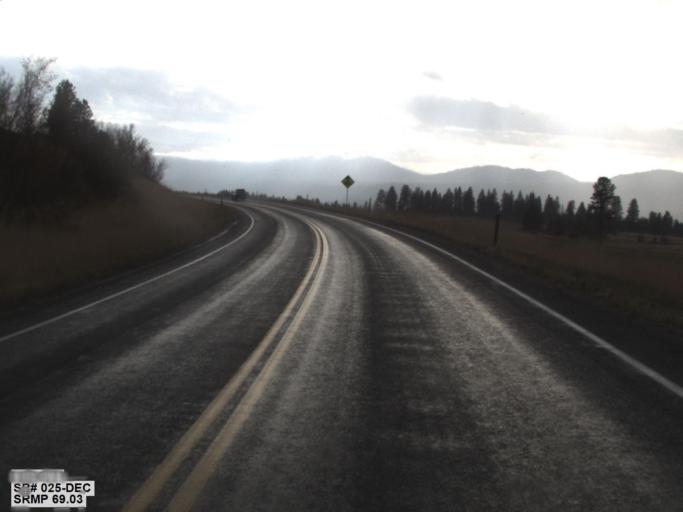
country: US
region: Washington
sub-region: Stevens County
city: Kettle Falls
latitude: 48.4659
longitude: -118.1794
